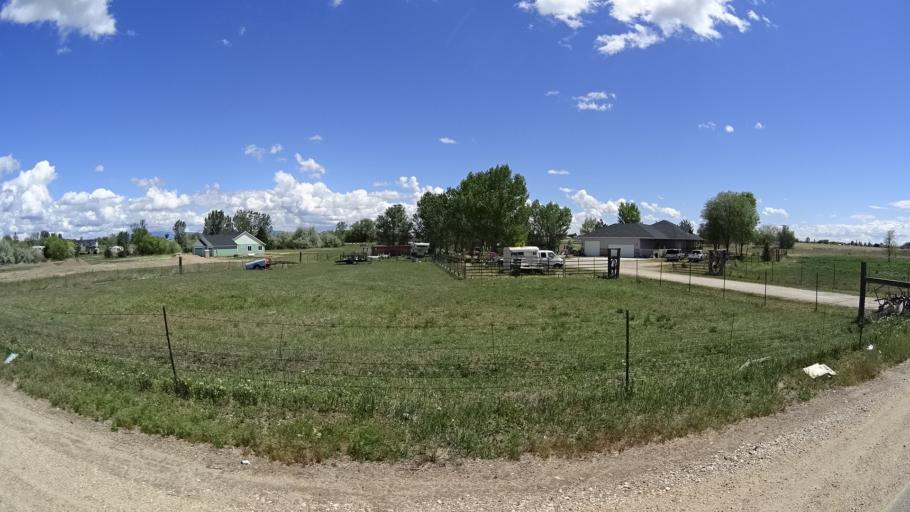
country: US
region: Idaho
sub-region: Ada County
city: Kuna
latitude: 43.5548
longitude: -116.4736
